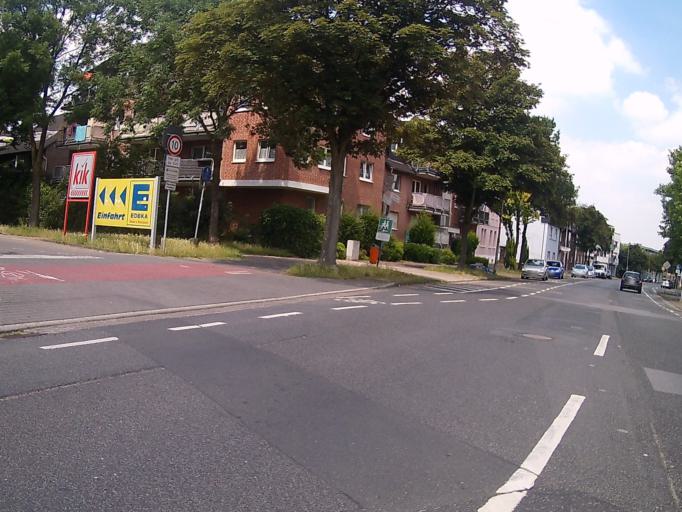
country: DE
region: North Rhine-Westphalia
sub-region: Regierungsbezirk Dusseldorf
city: Moers
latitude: 51.4141
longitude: 6.5947
